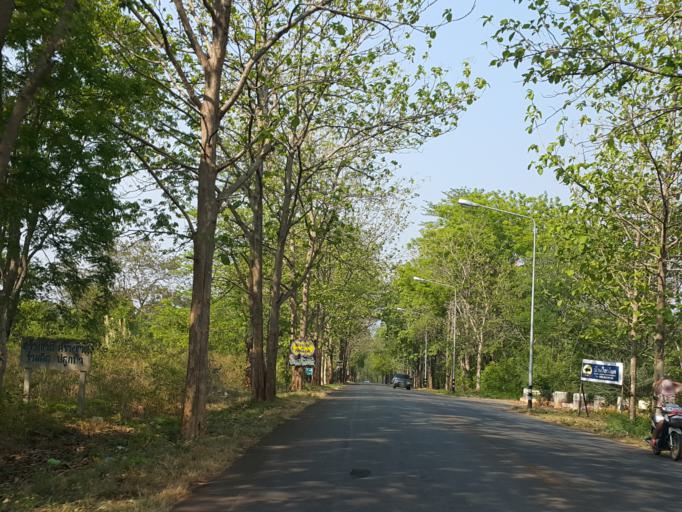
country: TH
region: Kanchanaburi
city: Sai Yok
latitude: 14.1289
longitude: 99.1621
